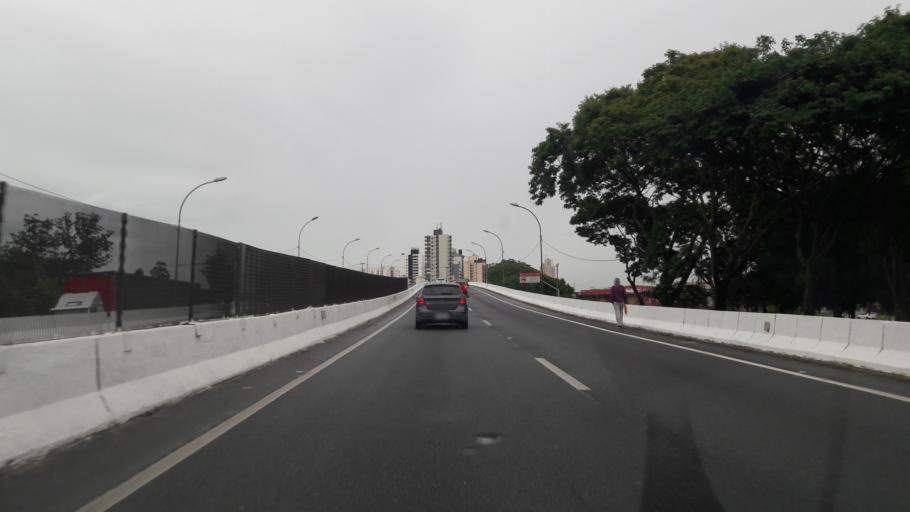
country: BR
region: Parana
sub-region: Pinhais
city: Pinhais
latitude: -25.4460
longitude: -49.2329
